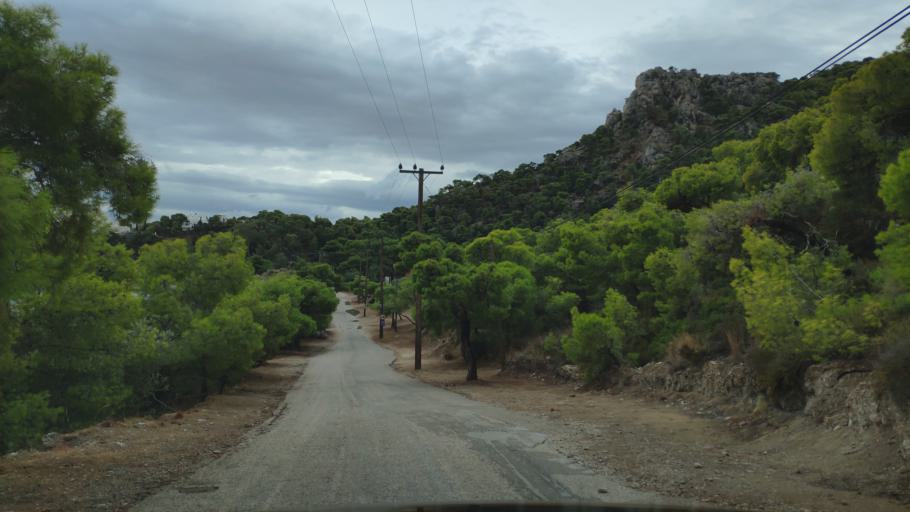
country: GR
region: Peloponnese
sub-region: Nomos Korinthias
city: Perachora
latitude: 38.0295
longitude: 22.8723
